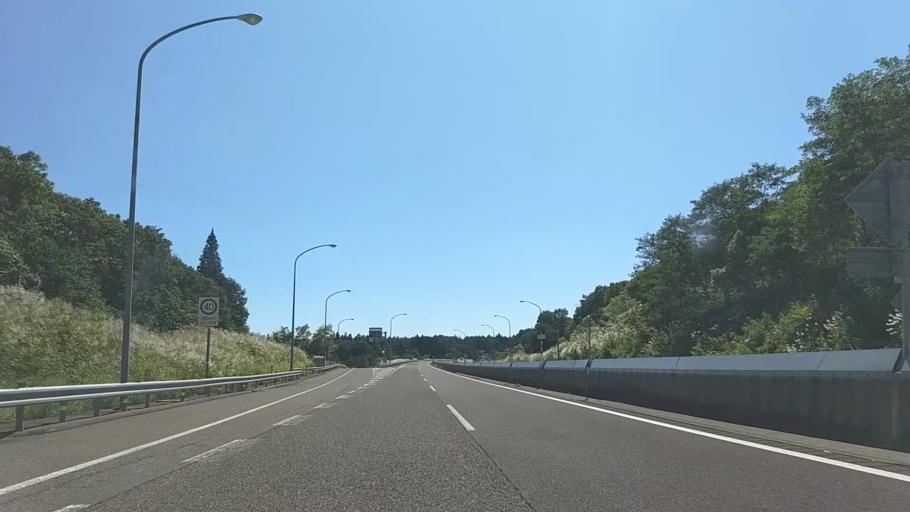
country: JP
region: Niigata
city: Arai
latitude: 36.8698
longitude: 138.1949
